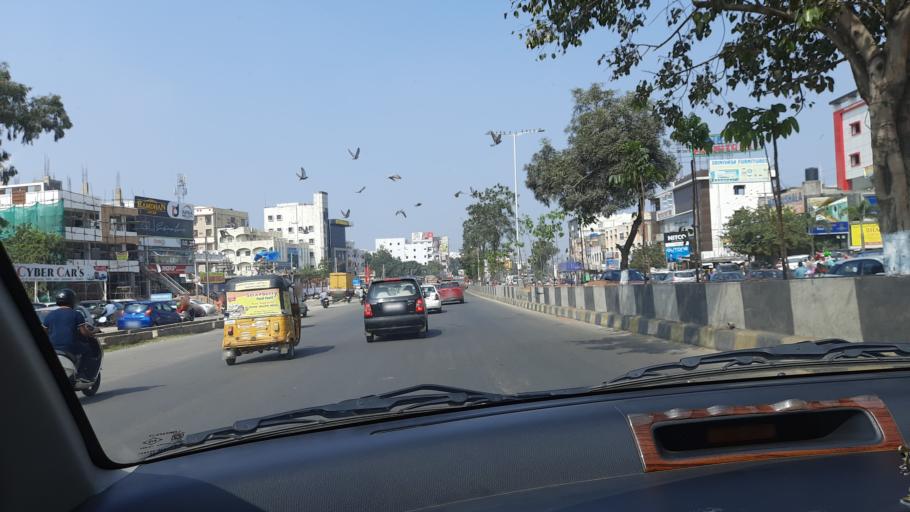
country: IN
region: Telangana
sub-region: Rangareddi
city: Lal Bahadur Nagar
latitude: 17.3630
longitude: 78.5573
